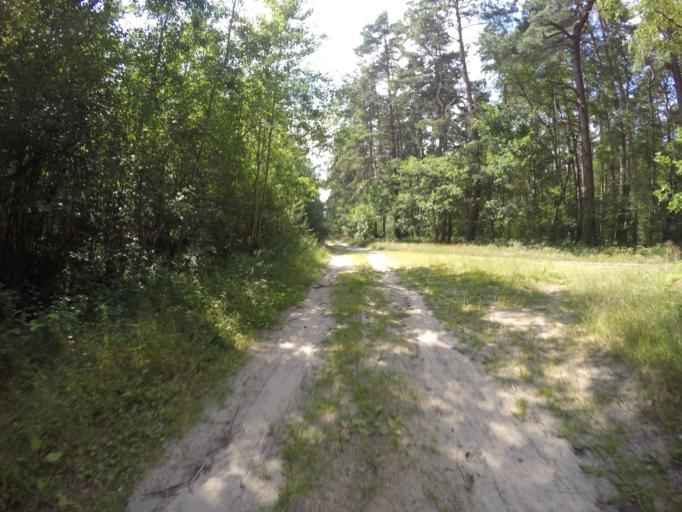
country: DE
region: Lower Saxony
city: Dahlem
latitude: 53.2438
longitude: 10.7463
